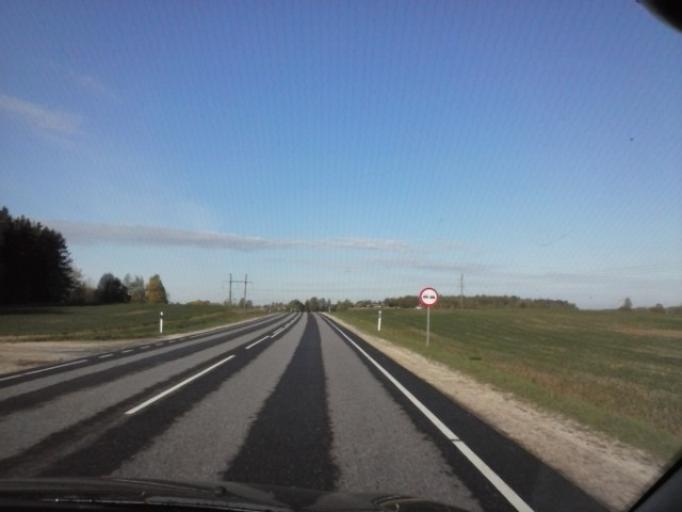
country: EE
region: Tartu
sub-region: Elva linn
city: Elva
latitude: 58.1523
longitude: 26.2689
